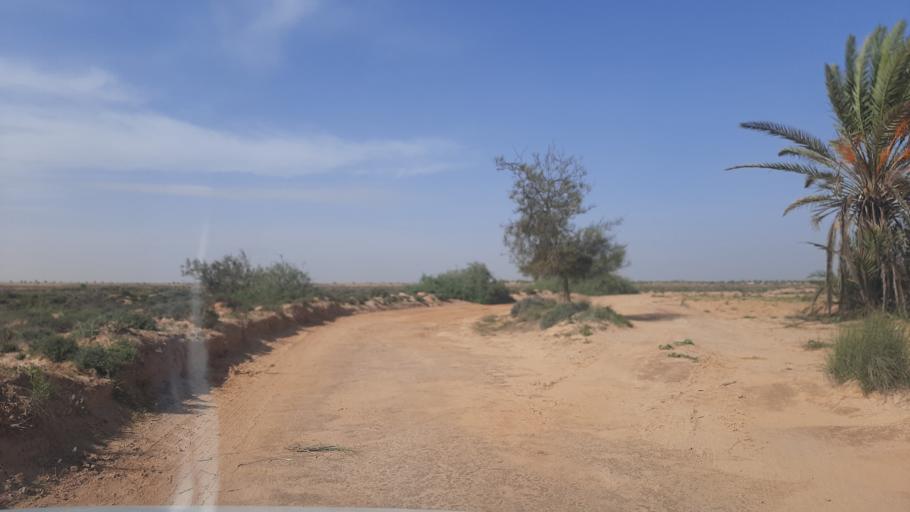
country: TN
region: Madanin
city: Zarzis
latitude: 33.4456
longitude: 10.8081
